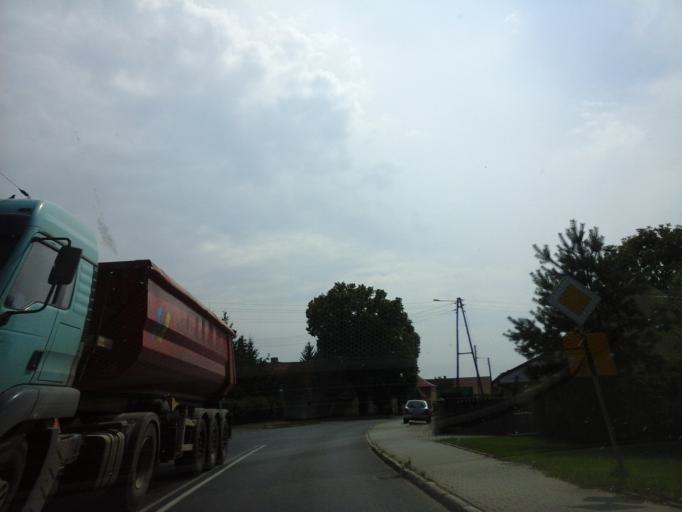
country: PL
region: Lower Silesian Voivodeship
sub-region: Powiat strzelinski
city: Strzelin
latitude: 50.8687
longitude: 17.0660
